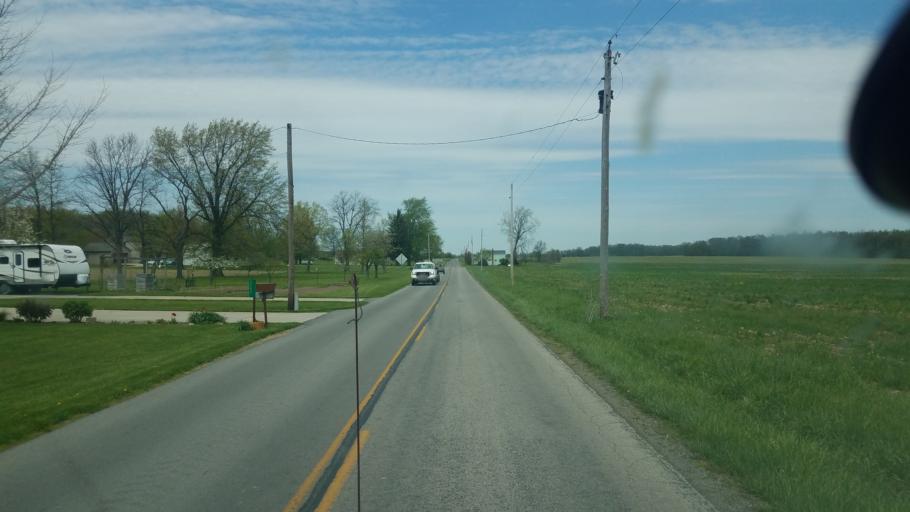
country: US
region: Ohio
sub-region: Allen County
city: Bluffton
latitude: 40.7854
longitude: -83.9701
